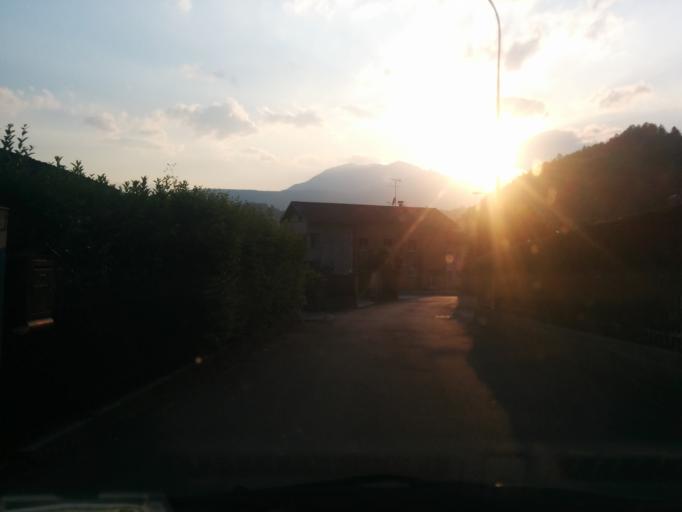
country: IT
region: Trentino-Alto Adige
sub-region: Provincia di Trento
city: Levico Terme
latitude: 46.0139
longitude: 11.2940
